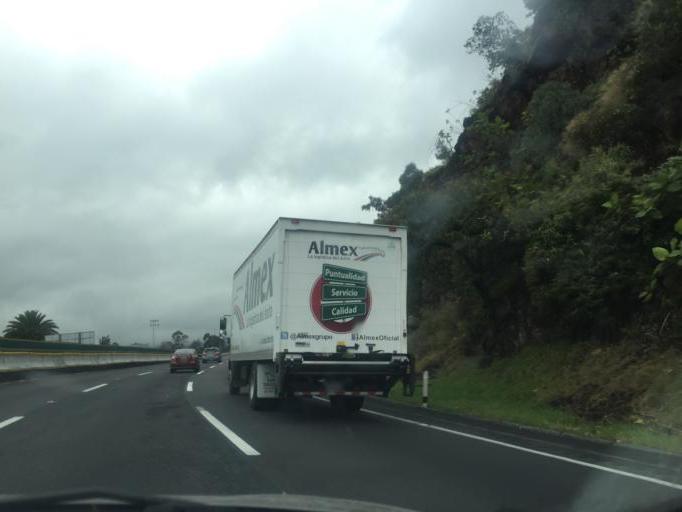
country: MX
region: Mexico City
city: Xochimilco
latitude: 19.2246
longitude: -99.1290
